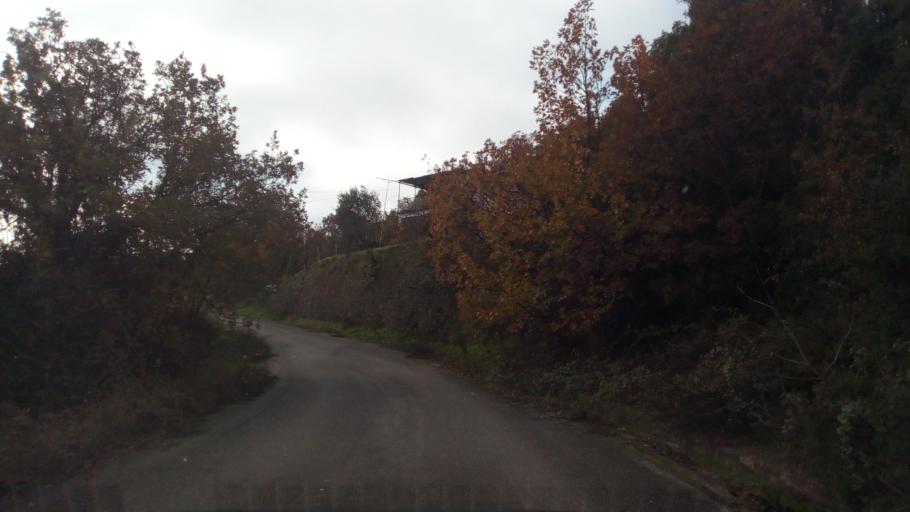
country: GR
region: West Greece
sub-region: Nomos Aitolias kai Akarnanias
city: Nafpaktos
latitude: 38.5260
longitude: 21.9778
